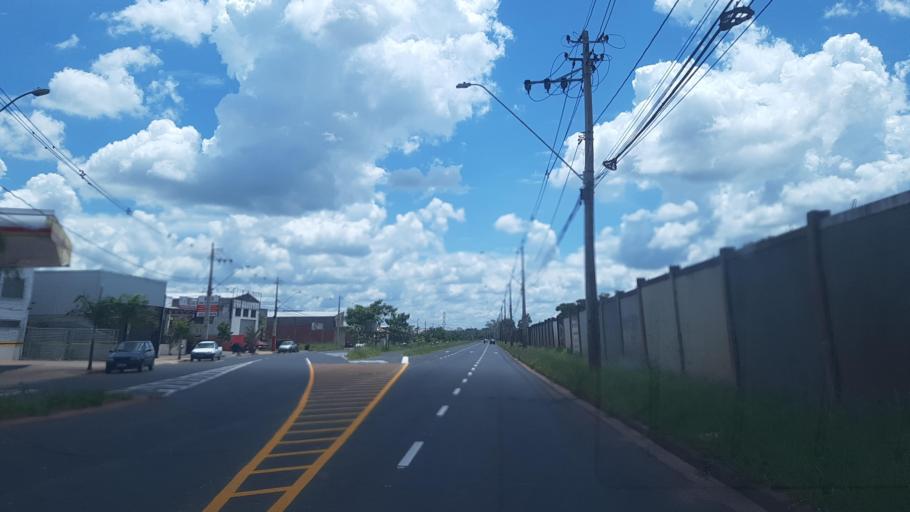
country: BR
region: Minas Gerais
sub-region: Uberlandia
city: Uberlandia
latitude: -18.9615
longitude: -48.3389
